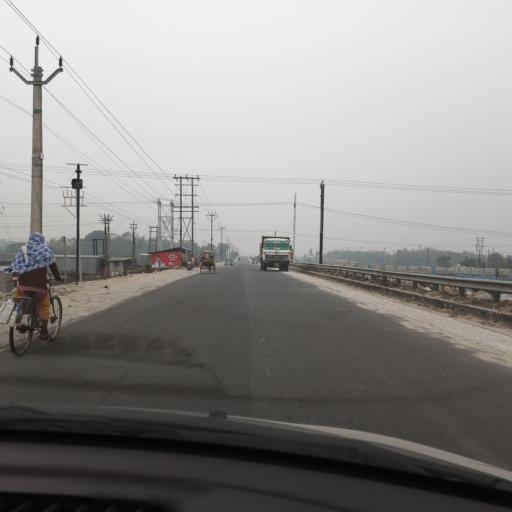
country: IN
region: West Bengal
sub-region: Darjiling
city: Shiliguri
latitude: 26.6605
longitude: 88.4600
